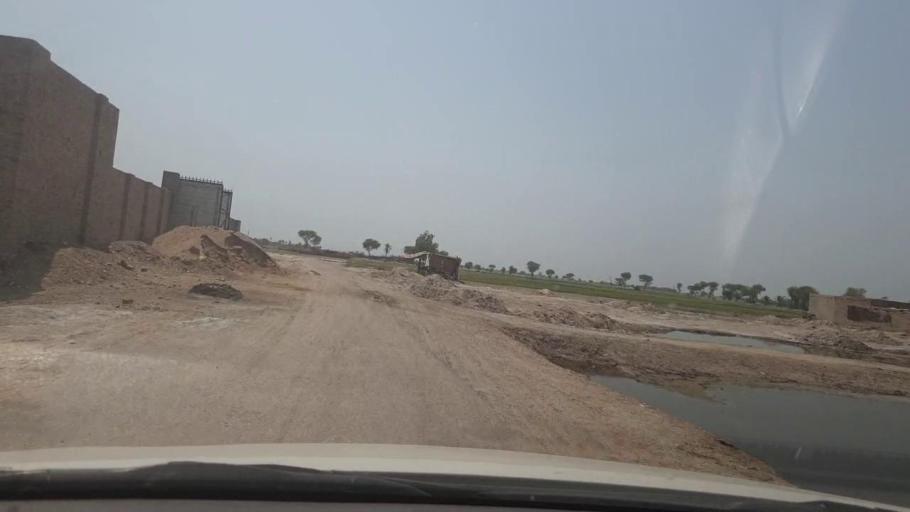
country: PK
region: Sindh
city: Shikarpur
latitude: 27.9934
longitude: 68.5733
